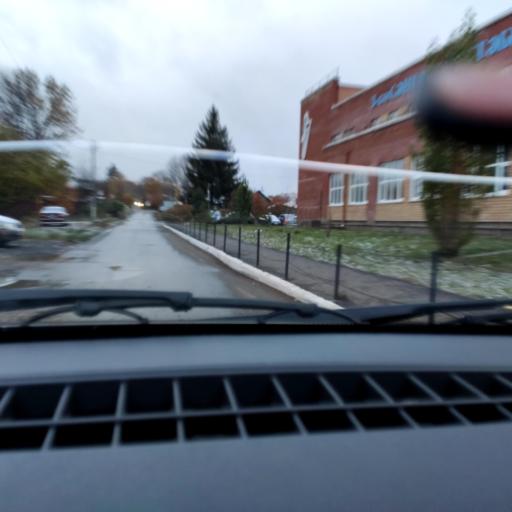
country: RU
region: Bashkortostan
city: Avdon
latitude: 54.6960
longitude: 55.8166
